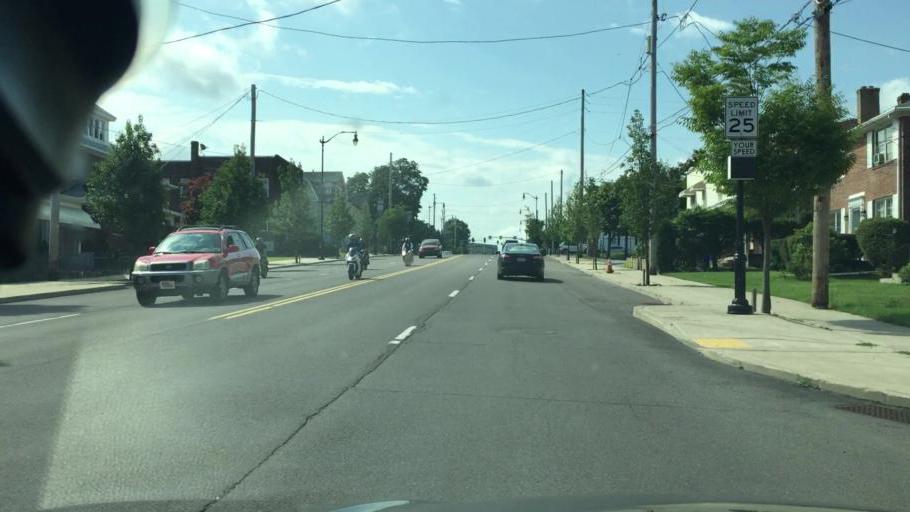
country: US
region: Pennsylvania
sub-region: Luzerne County
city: West Hazleton
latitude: 40.9626
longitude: -75.9967
